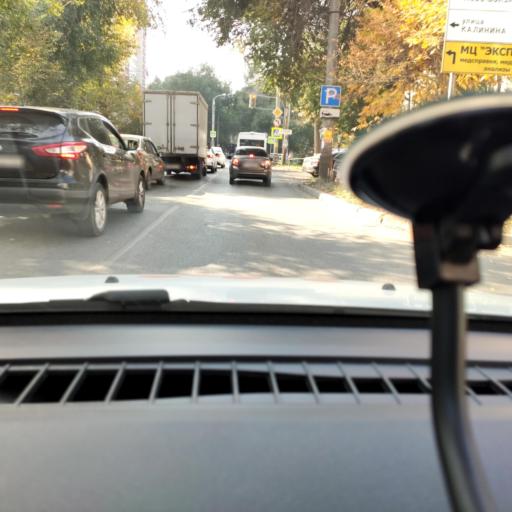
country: RU
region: Samara
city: Samara
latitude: 53.2214
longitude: 50.2475
